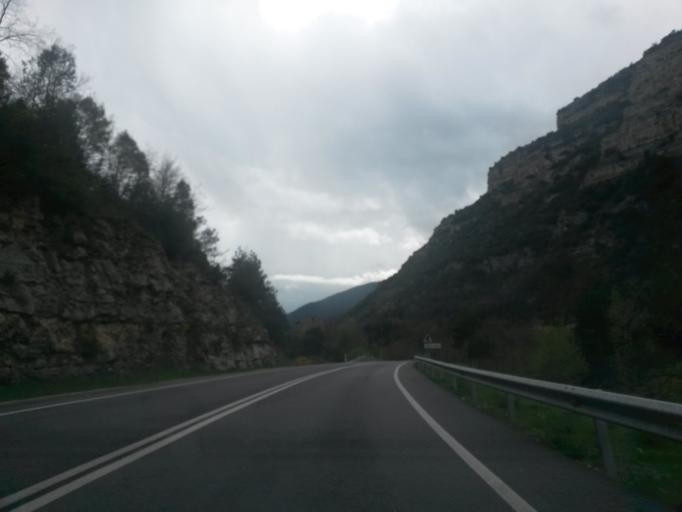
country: ES
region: Catalonia
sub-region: Provincia de Barcelona
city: Sant Julia de Cerdanyola
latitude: 42.1952
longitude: 1.8707
